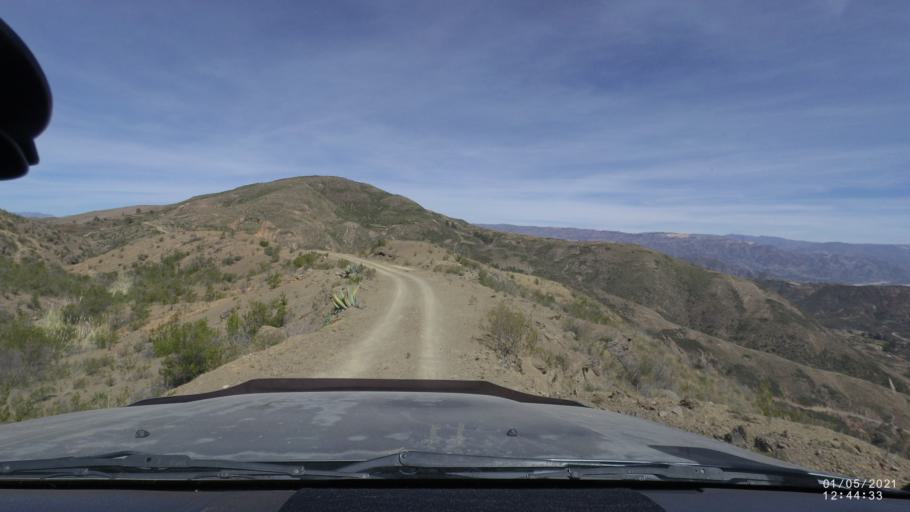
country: BO
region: Cochabamba
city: Capinota
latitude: -17.6831
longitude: -66.1605
